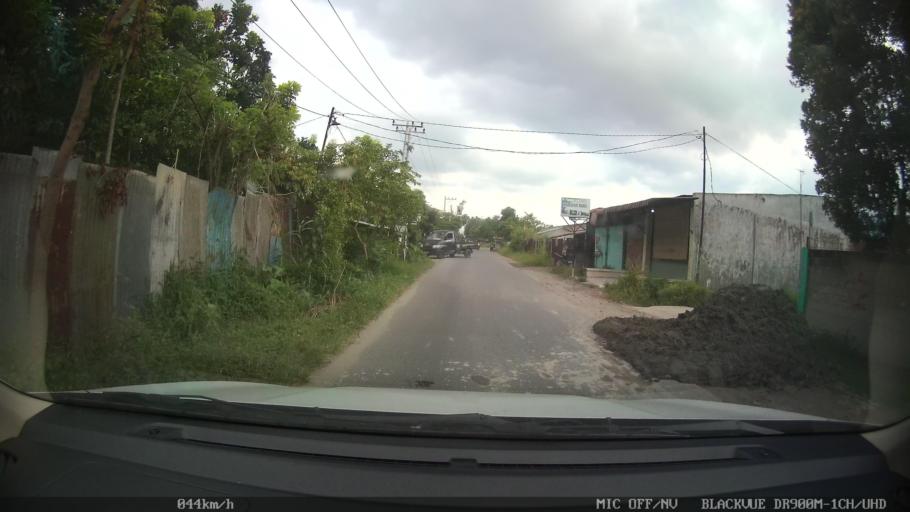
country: ID
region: North Sumatra
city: Sunggal
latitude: 3.6256
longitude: 98.6060
